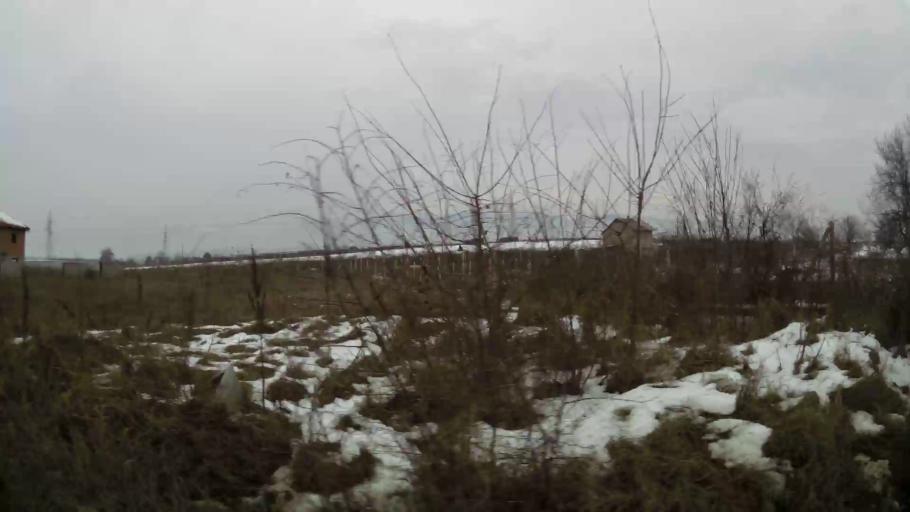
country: MK
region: Suto Orizari
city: Suto Orizare
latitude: 42.0438
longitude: 21.4353
